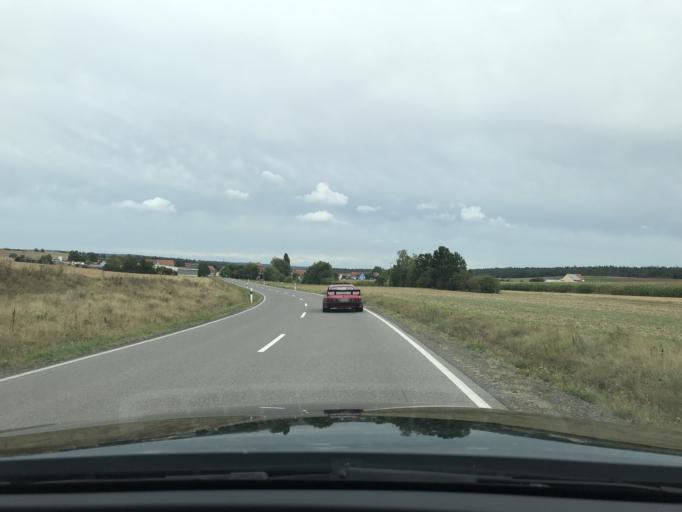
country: DE
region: Bavaria
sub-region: Regierungsbezirk Unterfranken
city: Burgpreppach
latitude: 50.1387
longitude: 10.6720
